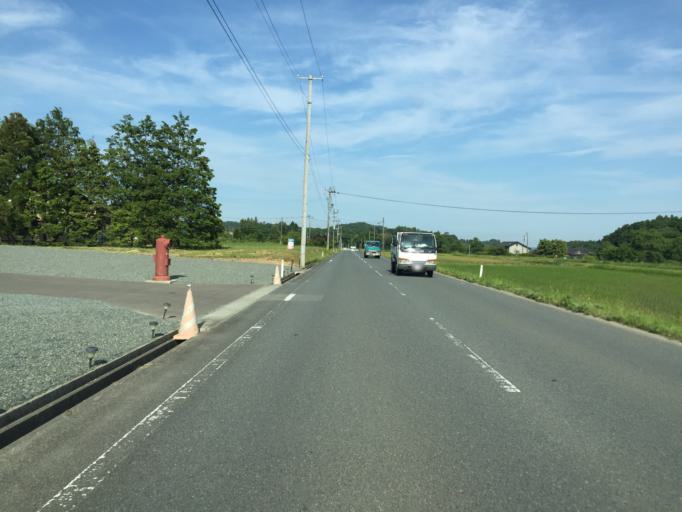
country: JP
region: Fukushima
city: Namie
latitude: 37.6641
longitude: 140.9576
